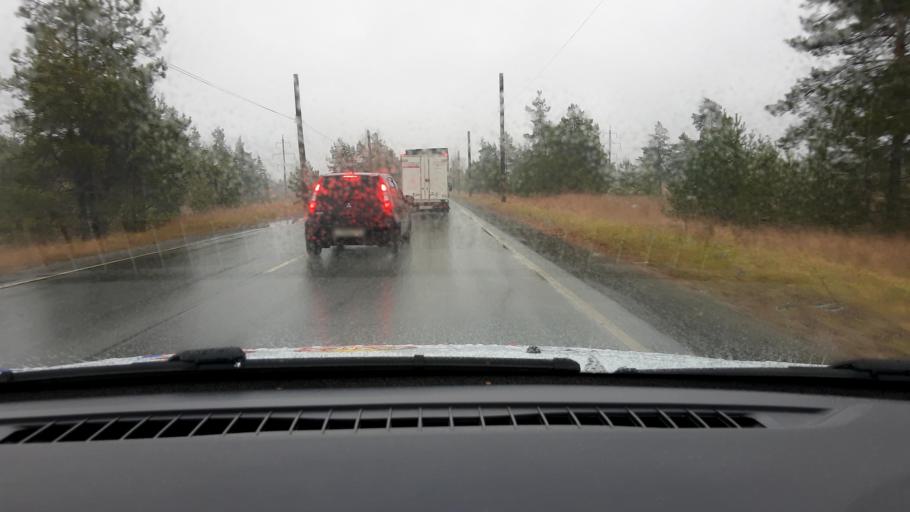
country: RU
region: Nizjnij Novgorod
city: Babino
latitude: 56.2810
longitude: 43.5712
